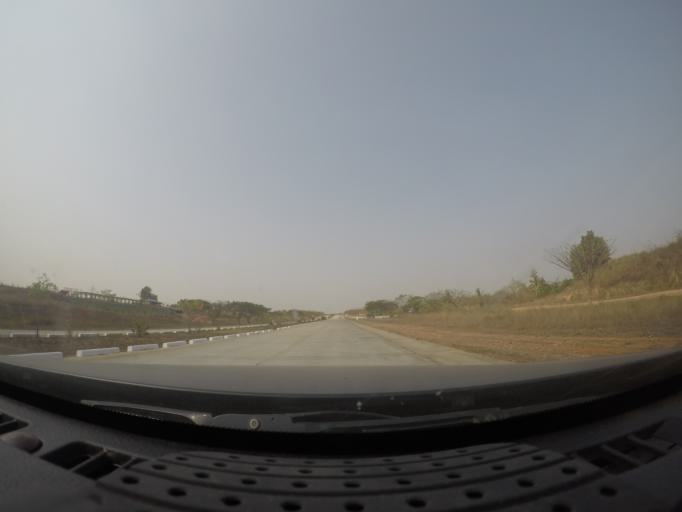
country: MM
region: Mandalay
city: Nay Pyi Taw
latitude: 19.9676
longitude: 95.9895
